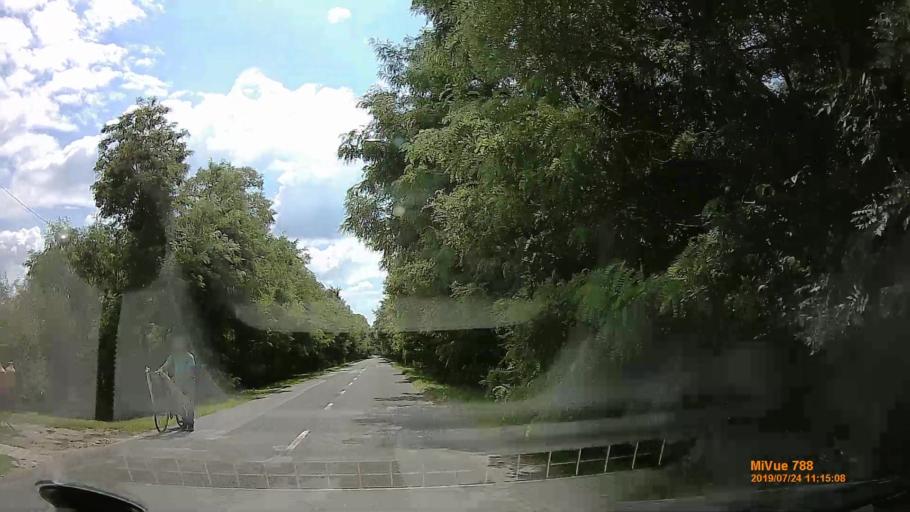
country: HU
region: Szabolcs-Szatmar-Bereg
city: Tarpa
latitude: 48.1939
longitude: 22.4542
